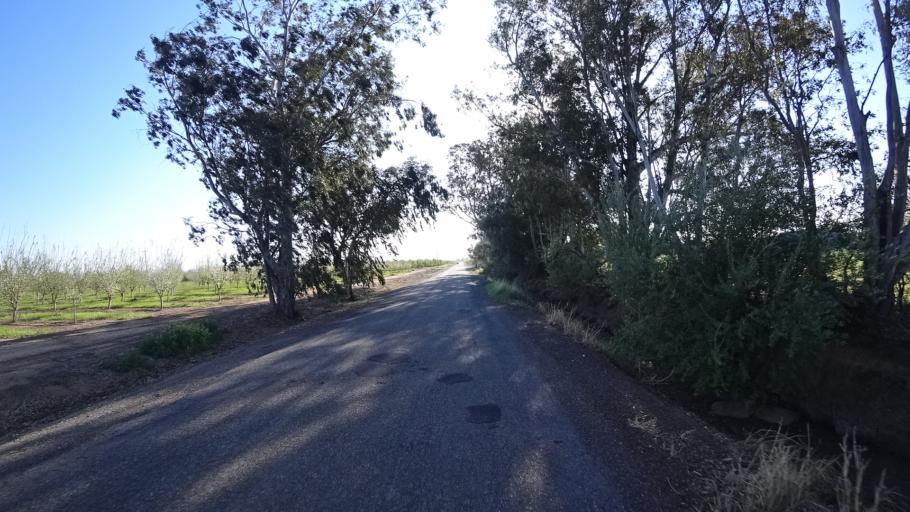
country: US
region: California
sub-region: Glenn County
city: Orland
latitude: 39.7976
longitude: -122.1427
